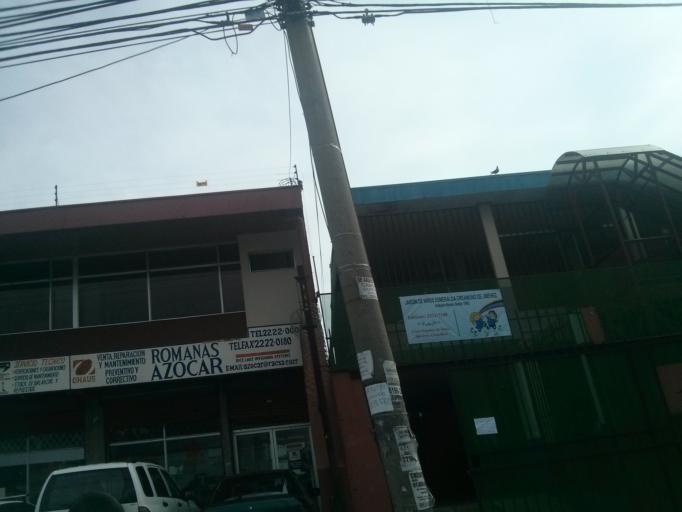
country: CR
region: San Jose
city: Colima
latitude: 9.9468
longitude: -84.0811
